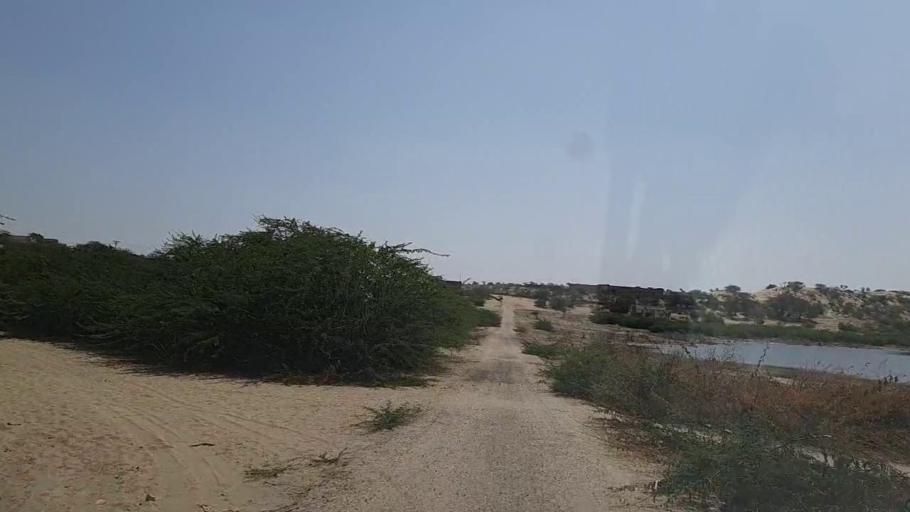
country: PK
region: Sindh
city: Diplo
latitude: 24.5124
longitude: 69.4138
